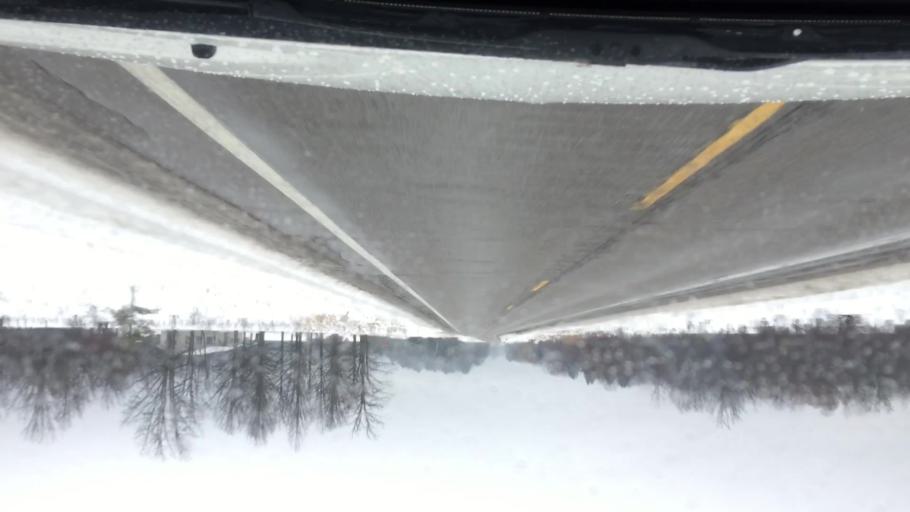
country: US
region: Michigan
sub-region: Charlevoix County
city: East Jordan
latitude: 45.1015
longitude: -85.1158
